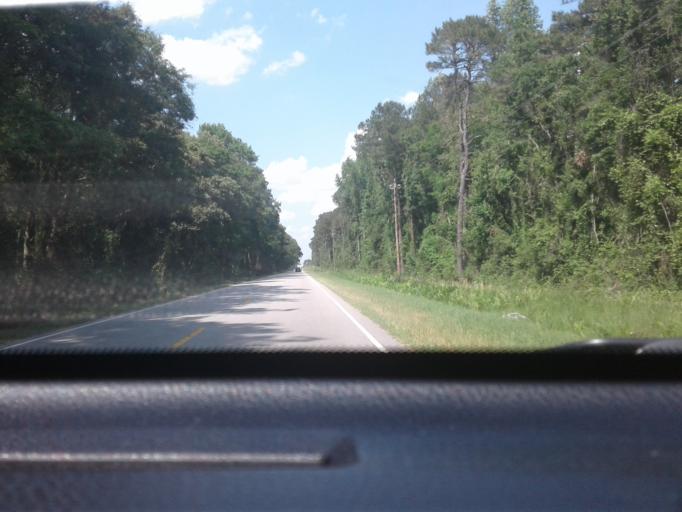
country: US
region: North Carolina
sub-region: Cumberland County
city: Eastover
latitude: 35.1882
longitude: -78.6994
